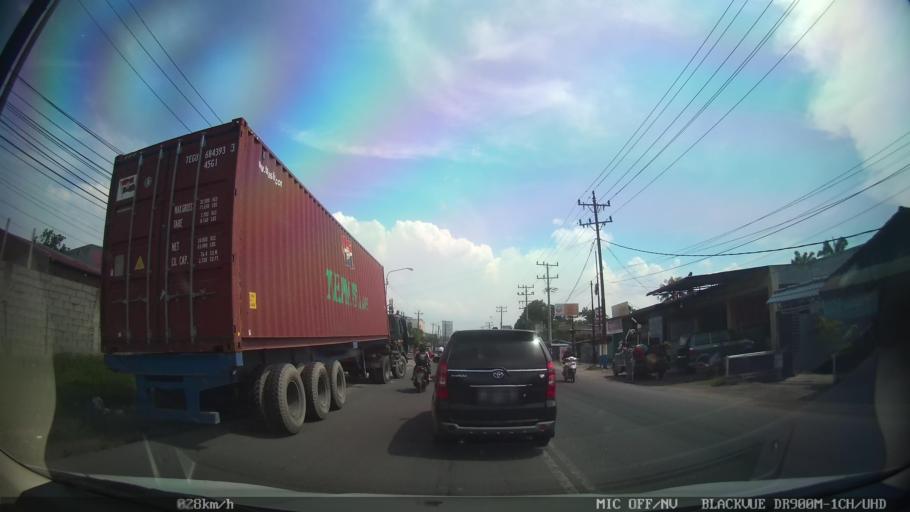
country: ID
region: North Sumatra
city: Labuhan Deli
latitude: 3.6631
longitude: 98.6563
